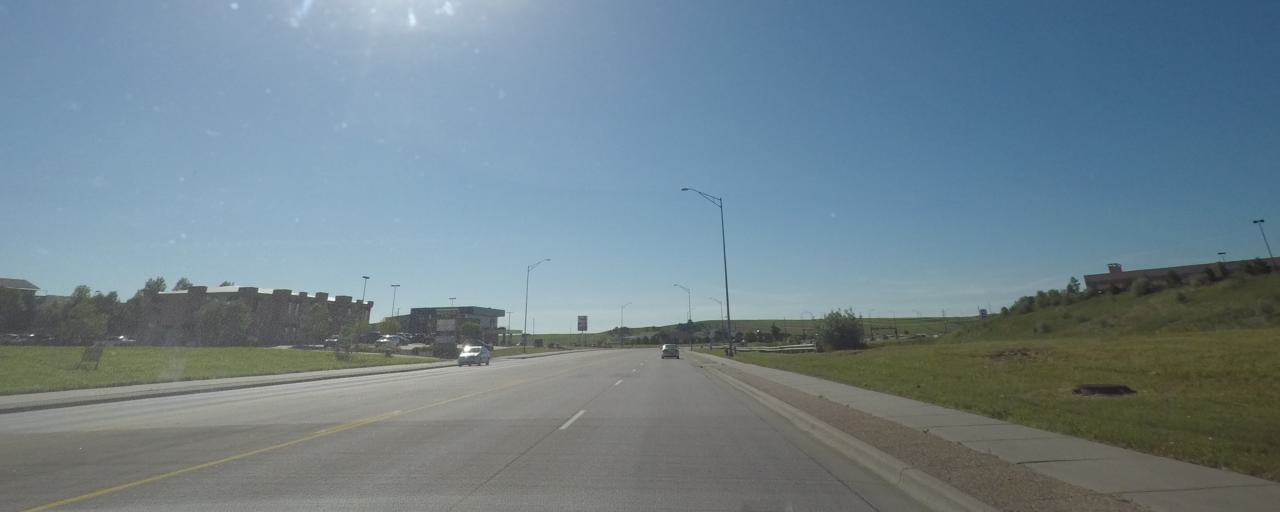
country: US
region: South Dakota
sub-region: Pennington County
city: Rapid City
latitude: 44.0353
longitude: -103.2156
